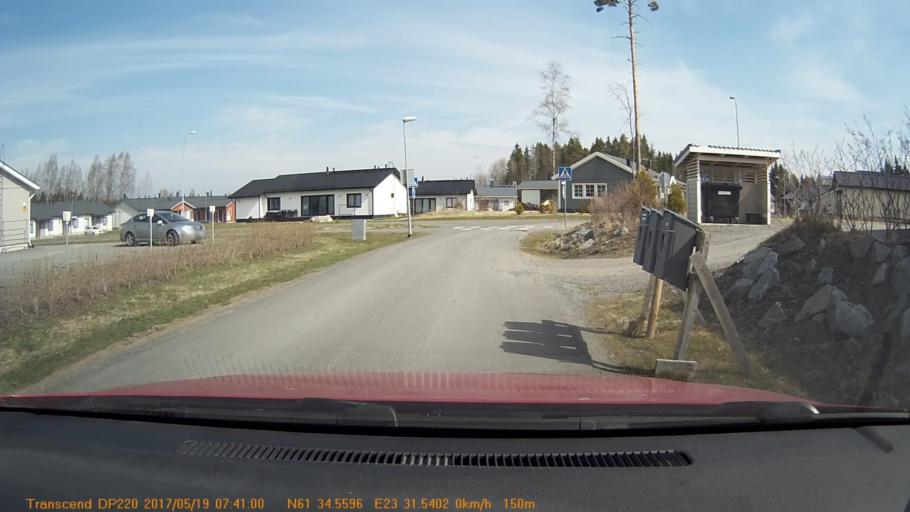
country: FI
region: Pirkanmaa
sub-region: Tampere
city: Yloejaervi
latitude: 61.5760
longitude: 23.5257
